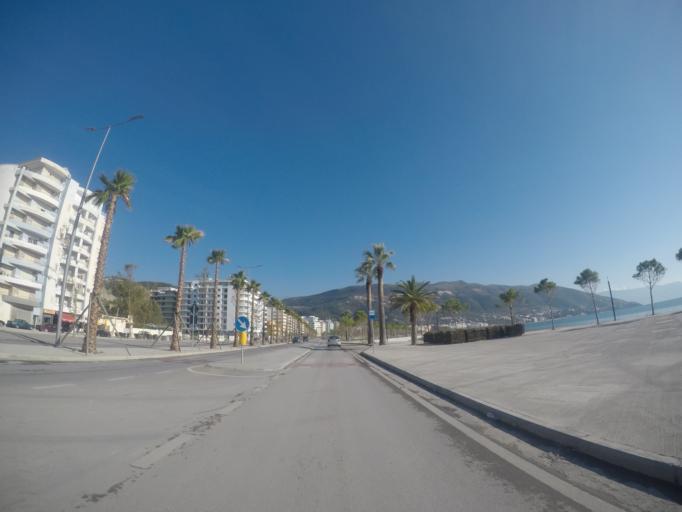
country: AL
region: Vlore
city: Vlore
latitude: 40.4507
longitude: 19.4894
